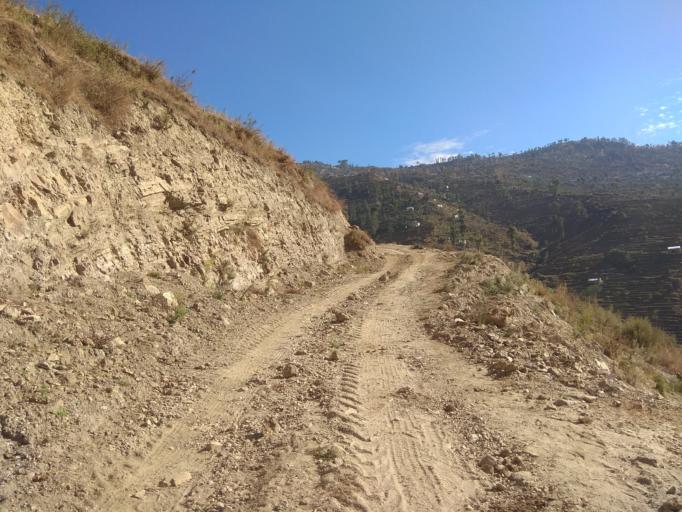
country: NP
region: Far Western
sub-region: Seti Zone
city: Achham
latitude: 29.2465
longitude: 81.6283
